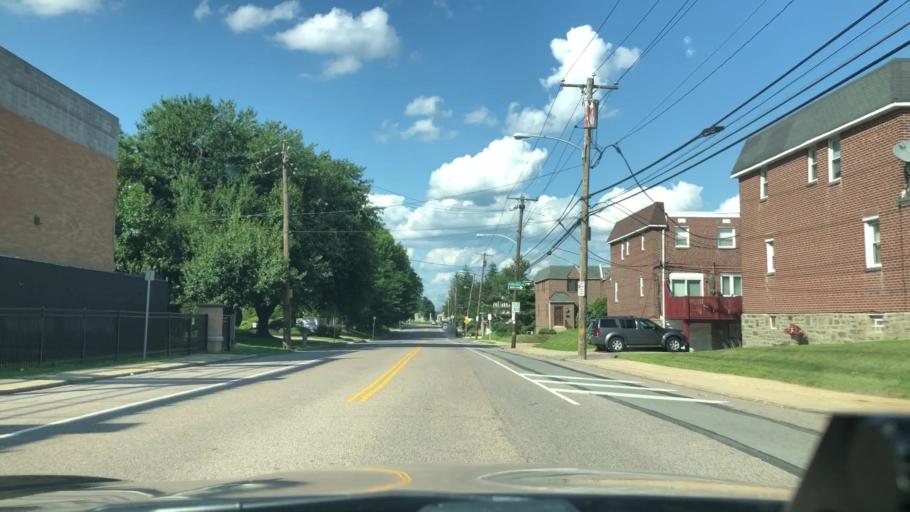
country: US
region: Pennsylvania
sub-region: Montgomery County
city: Wyndmoor
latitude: 40.0824
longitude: -75.1786
